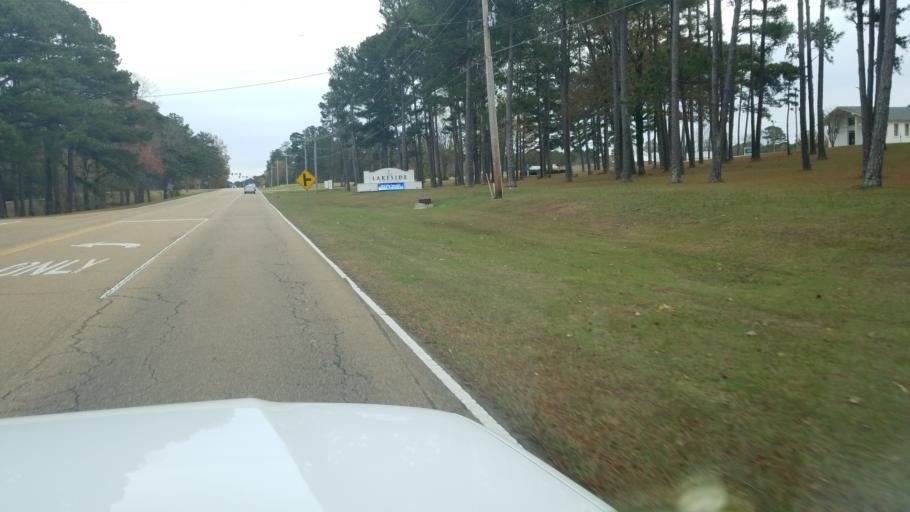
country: US
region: Mississippi
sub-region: Rankin County
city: Brandon
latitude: 32.3764
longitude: -90.0265
